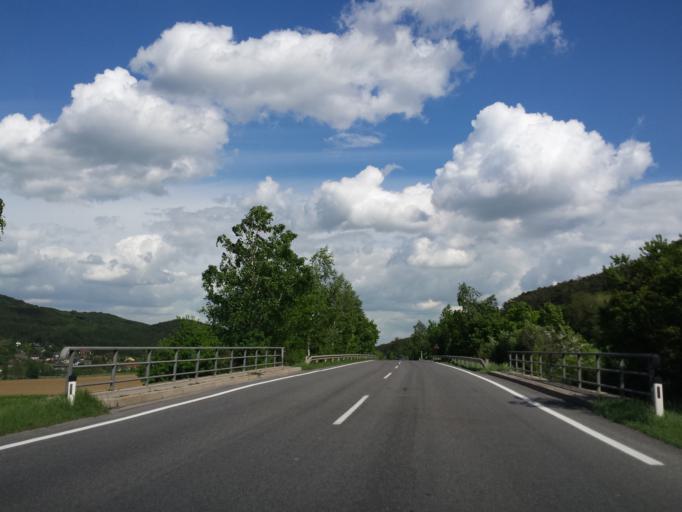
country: AT
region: Lower Austria
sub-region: Politischer Bezirk Baden
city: Hernstein
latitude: 47.8709
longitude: 16.0966
